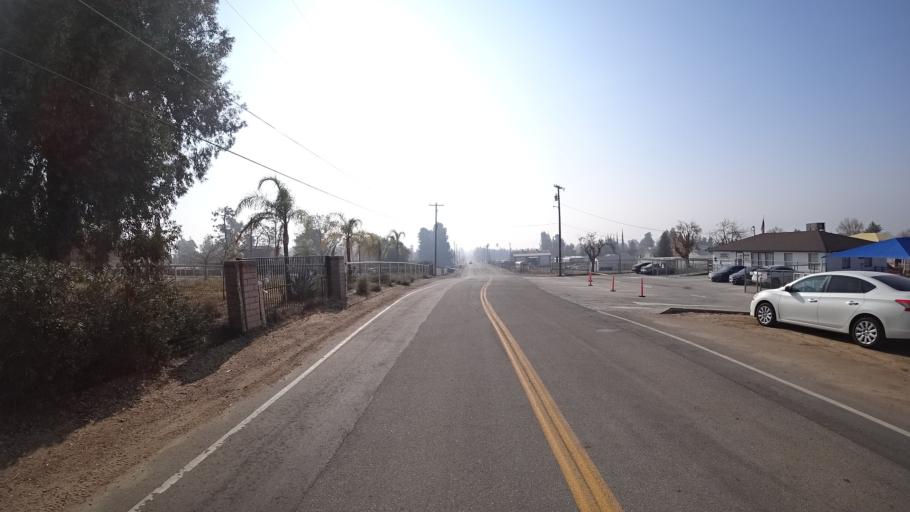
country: US
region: California
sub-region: Kern County
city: Lamont
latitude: 35.3672
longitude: -118.8964
